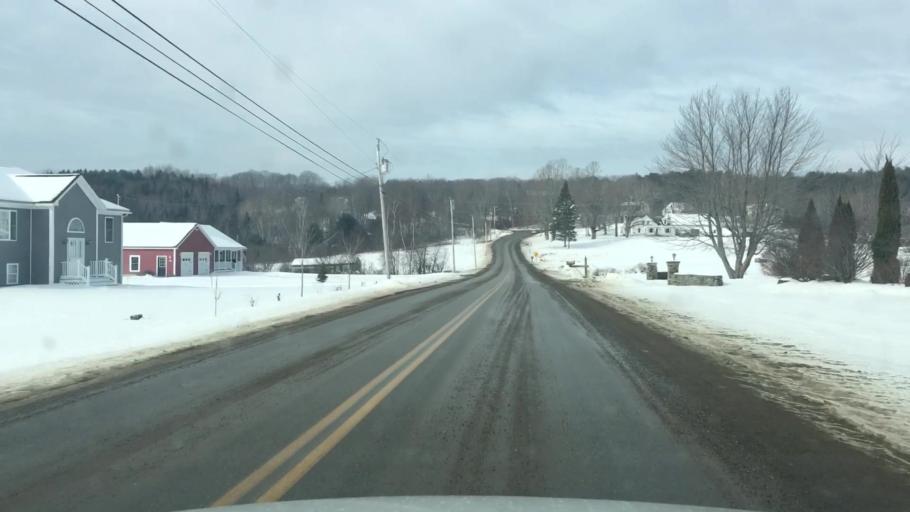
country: US
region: Maine
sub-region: Penobscot County
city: Hermon
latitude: 44.7666
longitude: -68.9571
